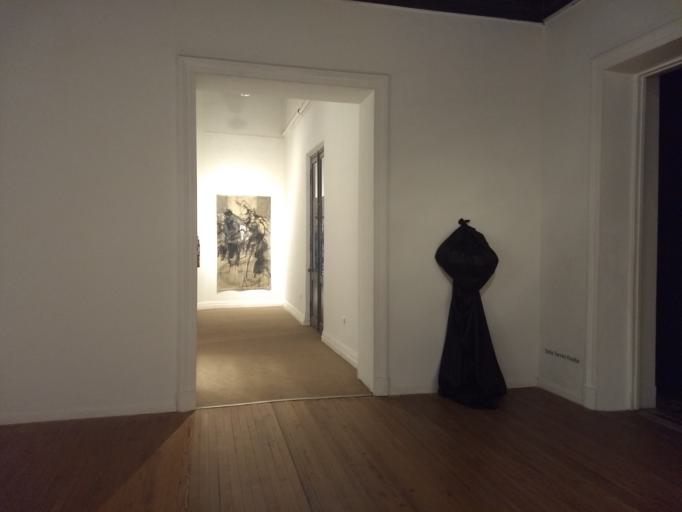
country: AR
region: Cordoba
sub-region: Departamento de Capital
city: Cordoba
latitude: -31.3734
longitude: -64.2552
